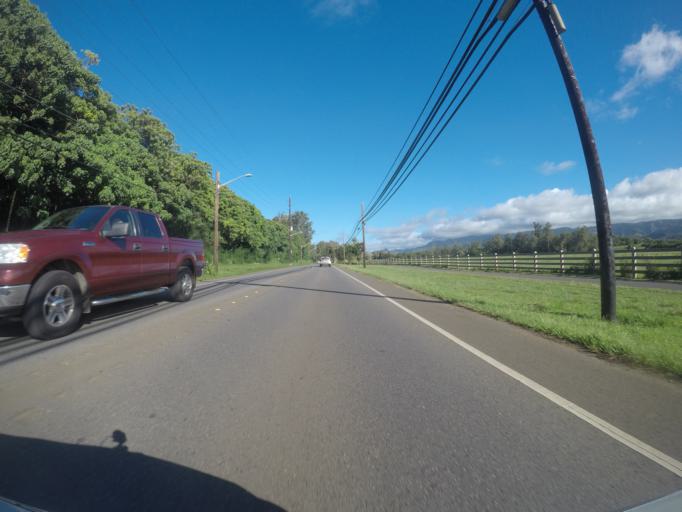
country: US
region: Hawaii
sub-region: Honolulu County
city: La'ie
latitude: 21.6594
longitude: -157.9328
